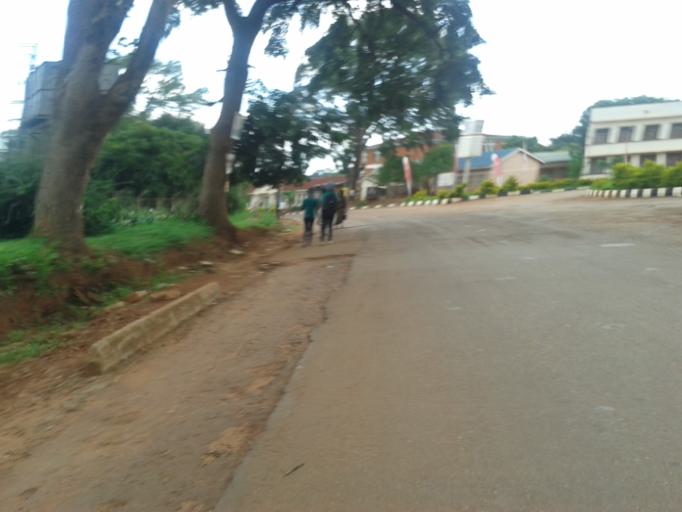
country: UG
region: Northern Region
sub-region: Gulu District
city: Gulu
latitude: 2.7792
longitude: 32.2973
